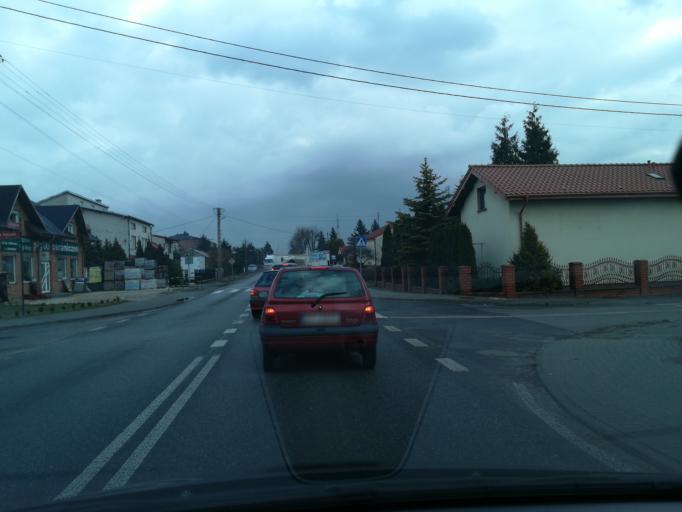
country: PL
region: Lodz Voivodeship
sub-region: Powiat radomszczanski
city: Radomsko
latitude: 51.0754
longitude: 19.4058
